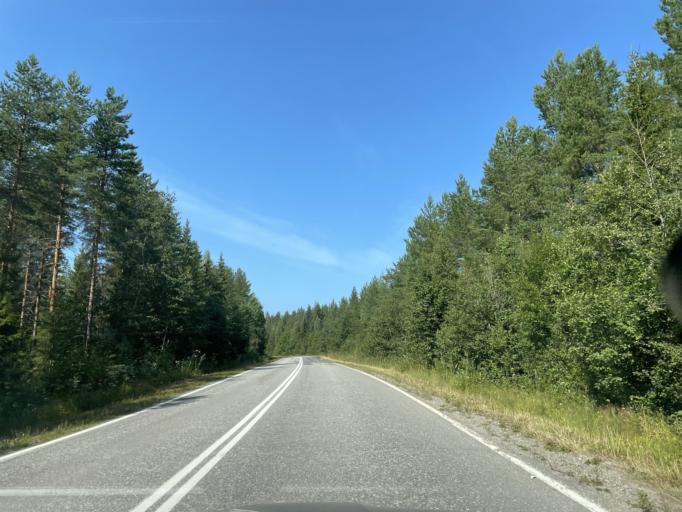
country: FI
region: Central Finland
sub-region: Saarijaervi-Viitasaari
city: Pihtipudas
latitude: 63.3652
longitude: 25.7128
